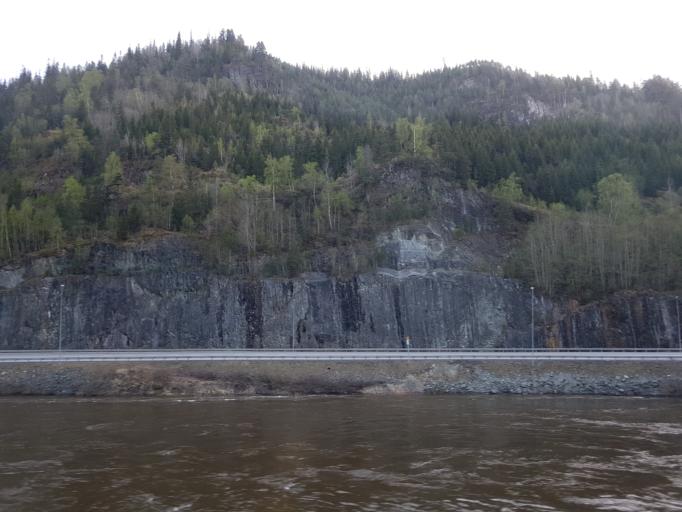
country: NO
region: Sor-Trondelag
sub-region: Midtre Gauldal
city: Storen
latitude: 63.0676
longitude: 10.2836
